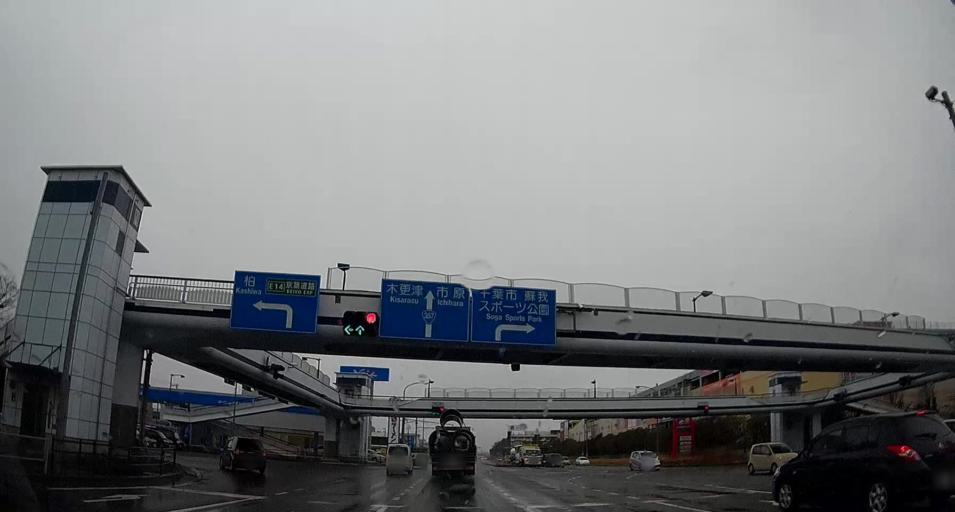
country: JP
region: Chiba
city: Chiba
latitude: 35.5870
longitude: 140.1240
